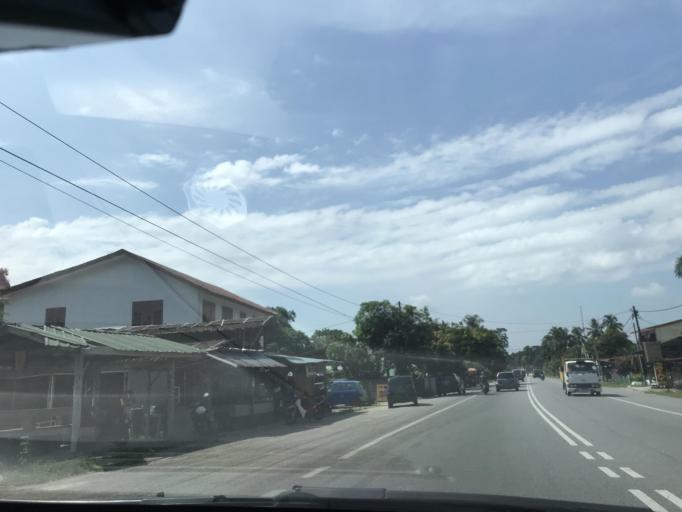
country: MY
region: Kelantan
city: Tumpat
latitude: 6.1356
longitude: 102.1740
